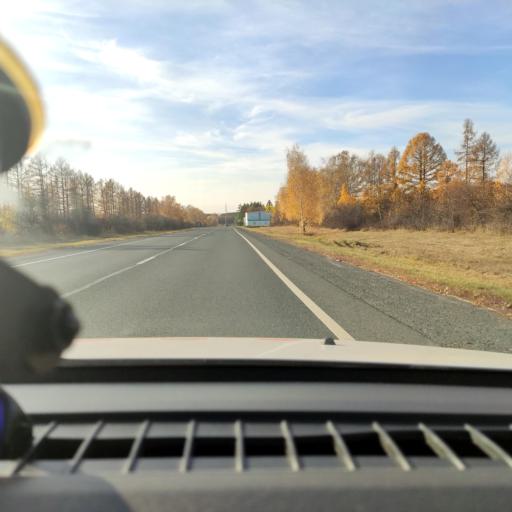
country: RU
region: Samara
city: Volzhskiy
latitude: 53.4582
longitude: 50.1268
